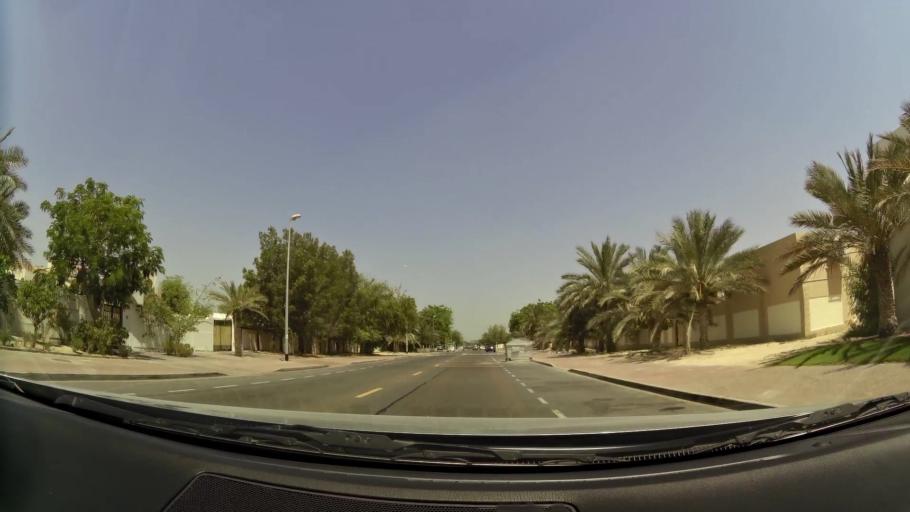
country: AE
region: Dubai
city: Dubai
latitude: 25.2125
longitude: 55.2667
